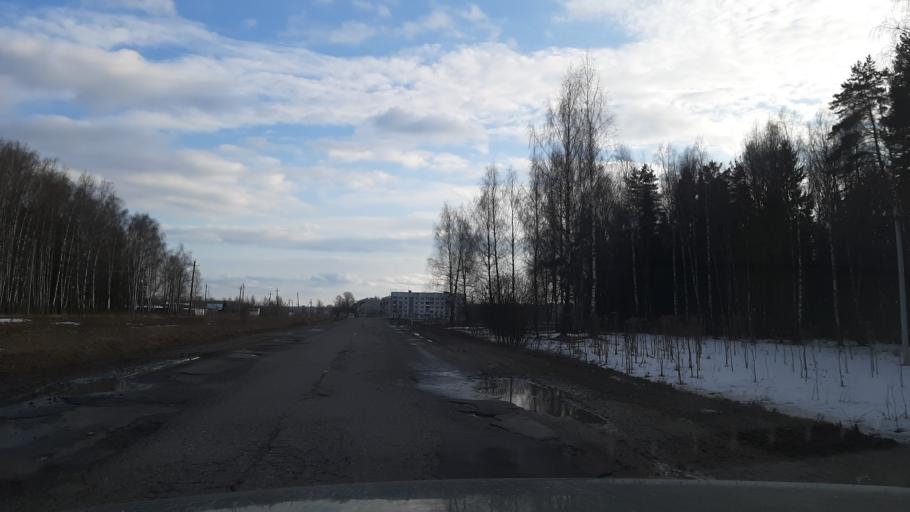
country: RU
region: Ivanovo
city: Novo-Talitsy
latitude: 56.9292
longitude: 40.7356
